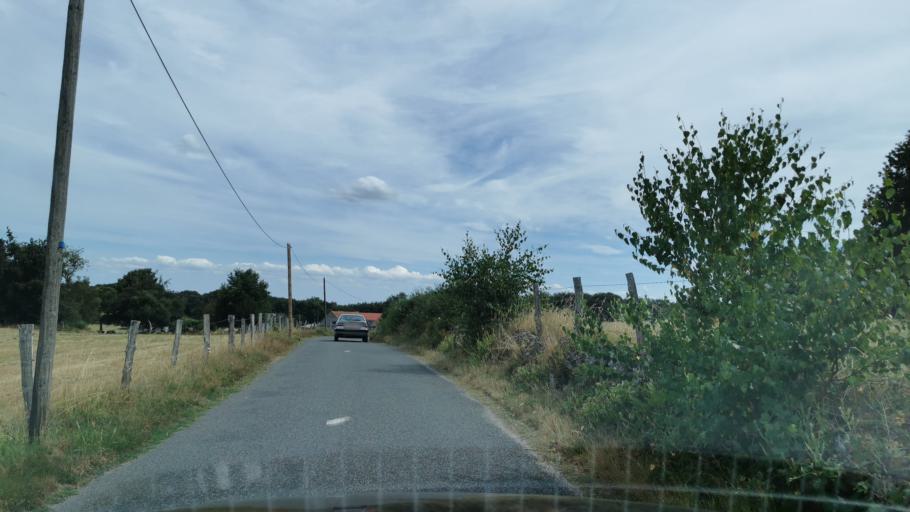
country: FR
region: Bourgogne
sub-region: Departement de Saone-et-Loire
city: Etang-sur-Arroux
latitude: 46.8039
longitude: 4.2601
